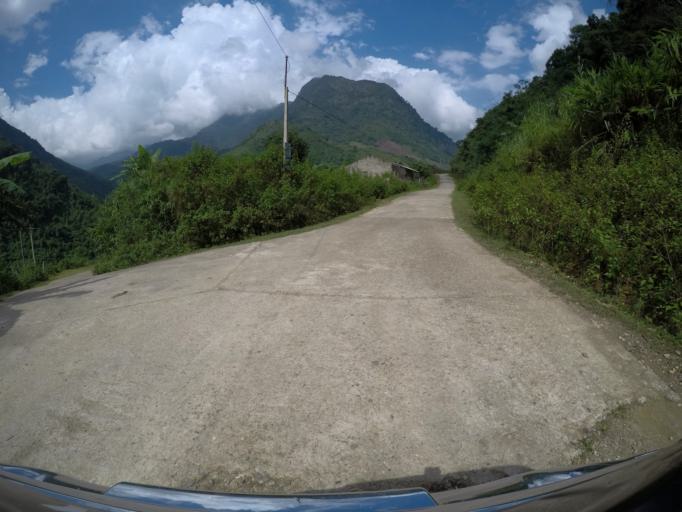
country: VN
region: Yen Bai
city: Son Thinh
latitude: 21.6798
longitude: 104.5462
